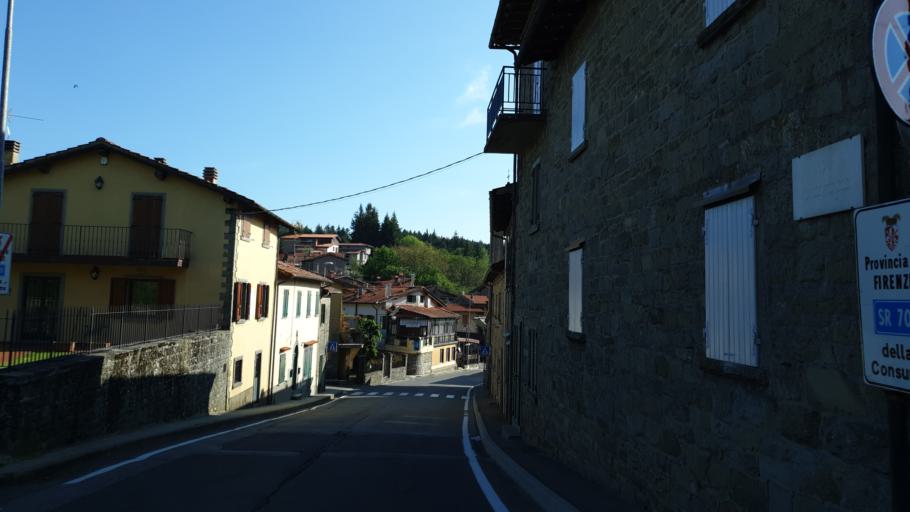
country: IT
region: Tuscany
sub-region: Province of Arezzo
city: Montemignaio
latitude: 43.7820
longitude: 11.5977
